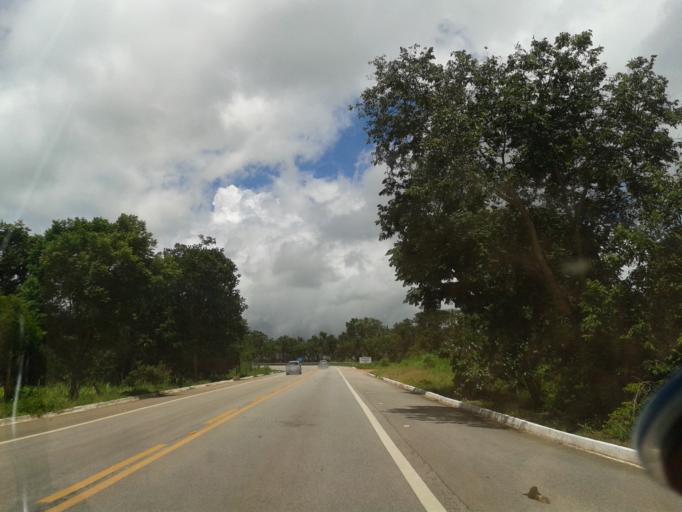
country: BR
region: Goias
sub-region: Goias
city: Goias
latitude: -15.8691
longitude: -50.0898
